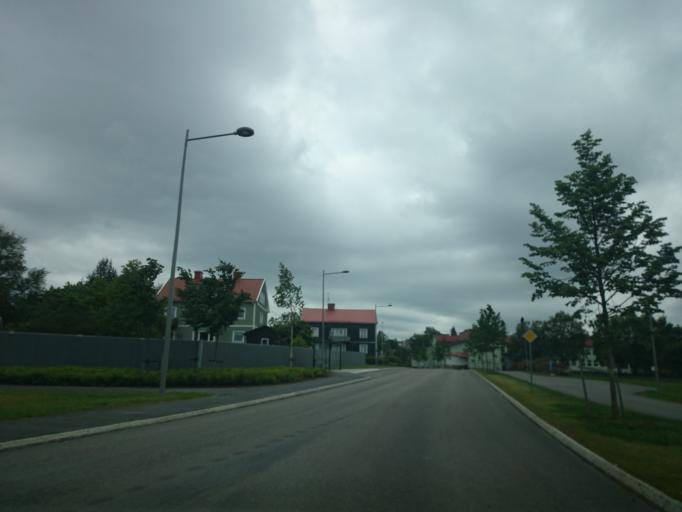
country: SE
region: Vaesternorrland
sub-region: Haernoesands Kommun
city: Haernoesand
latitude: 62.6373
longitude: 17.9255
